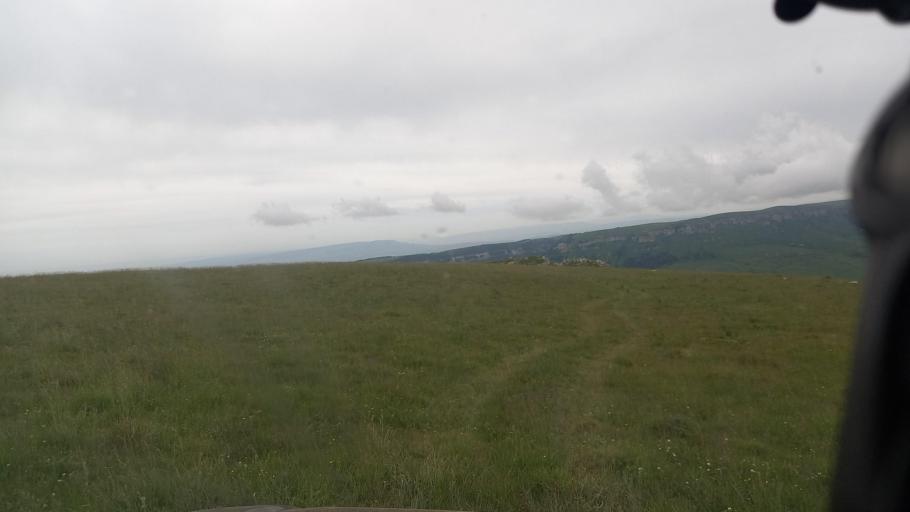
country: RU
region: Karachayevo-Cherkesiya
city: Pregradnaya
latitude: 43.9817
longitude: 41.3043
